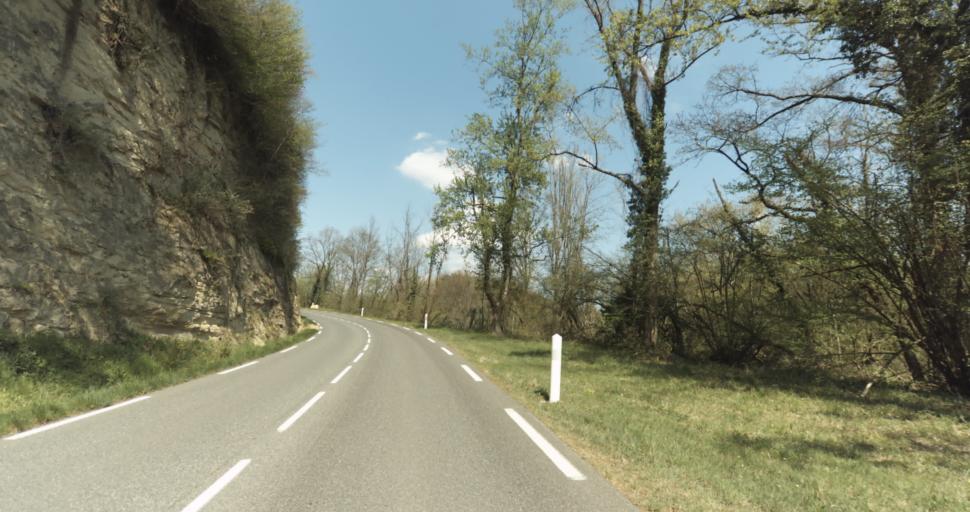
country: FR
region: Rhone-Alpes
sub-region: Departement de l'Isere
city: Saint-Romans
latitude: 45.1279
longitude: 5.3248
